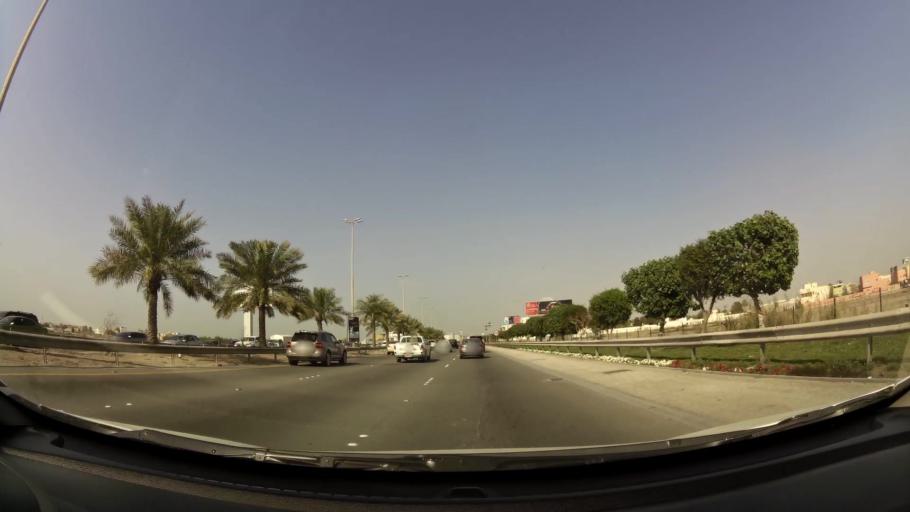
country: BH
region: Manama
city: Jidd Hafs
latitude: 26.2058
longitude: 50.5153
